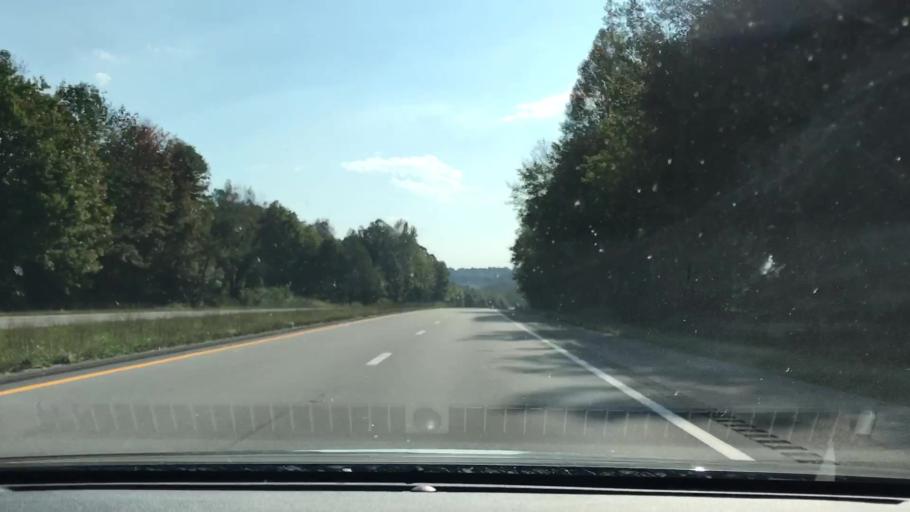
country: US
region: Kentucky
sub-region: Russell County
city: Russell Springs
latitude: 37.0619
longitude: -85.1846
